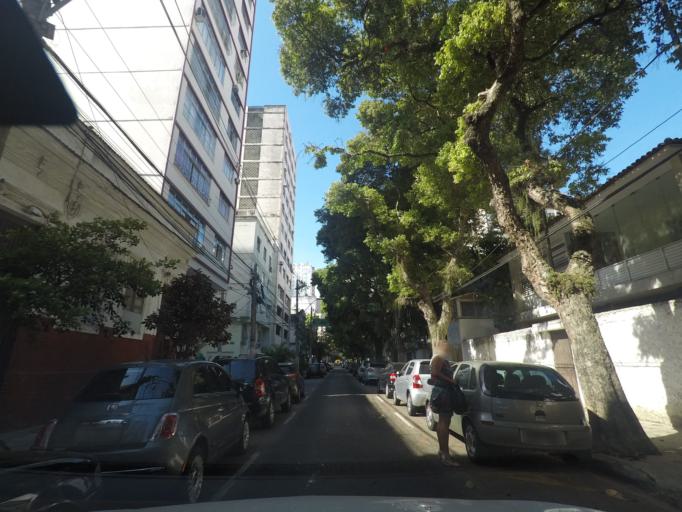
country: BR
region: Rio de Janeiro
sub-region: Niteroi
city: Niteroi
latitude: -22.9046
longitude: -43.1243
